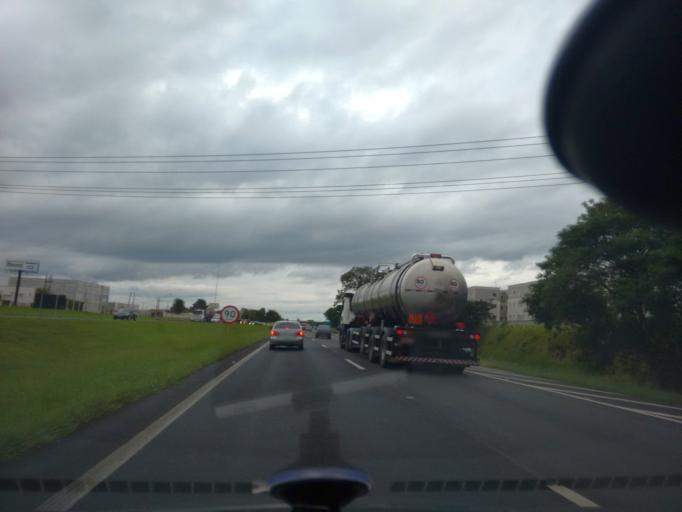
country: BR
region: Sao Paulo
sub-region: Rio Claro
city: Rio Claro
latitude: -22.4407
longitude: -47.5664
